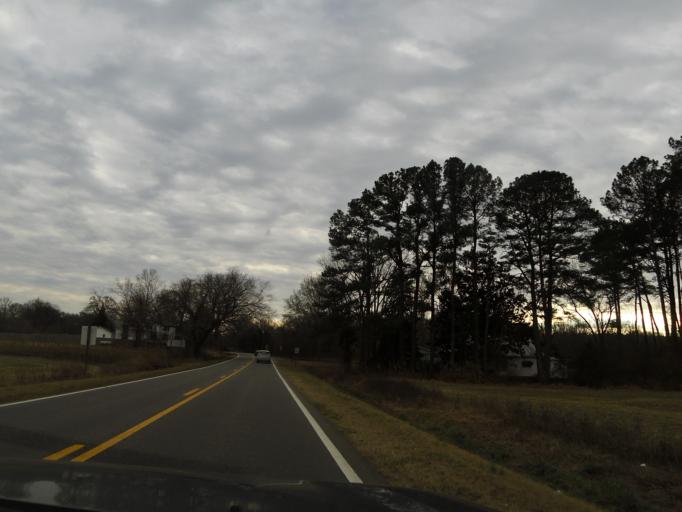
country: US
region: North Carolina
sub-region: Edgecombe County
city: Tarboro
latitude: 36.0183
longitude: -77.5001
